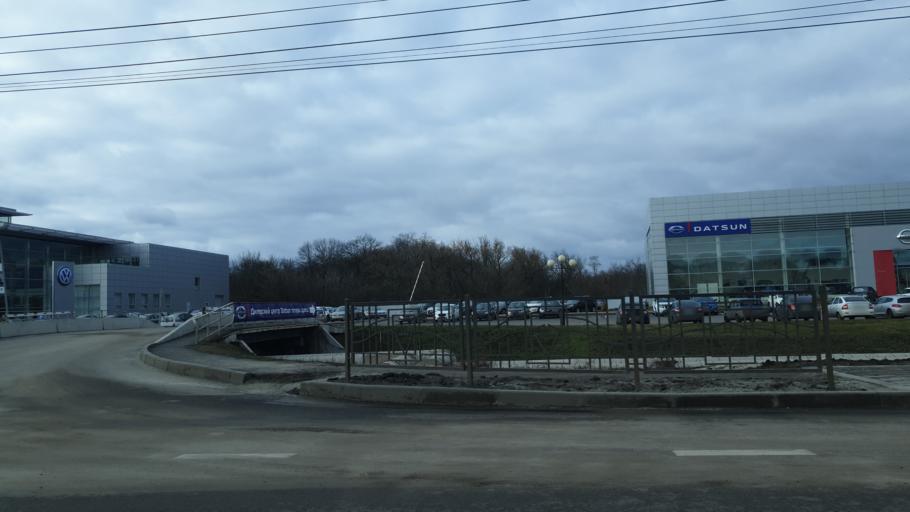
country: RU
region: Kursk
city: Kursk
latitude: 51.6887
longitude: 36.1537
